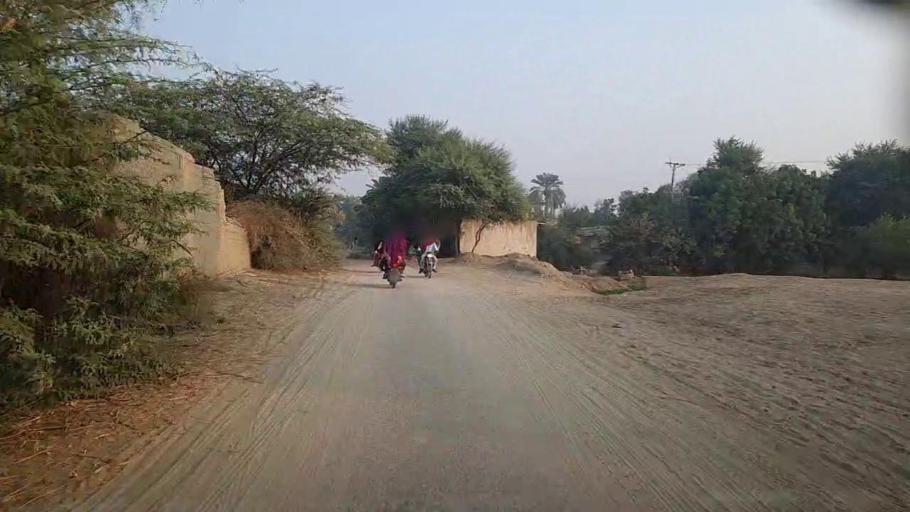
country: PK
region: Sindh
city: Bozdar
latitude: 27.0828
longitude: 68.5669
